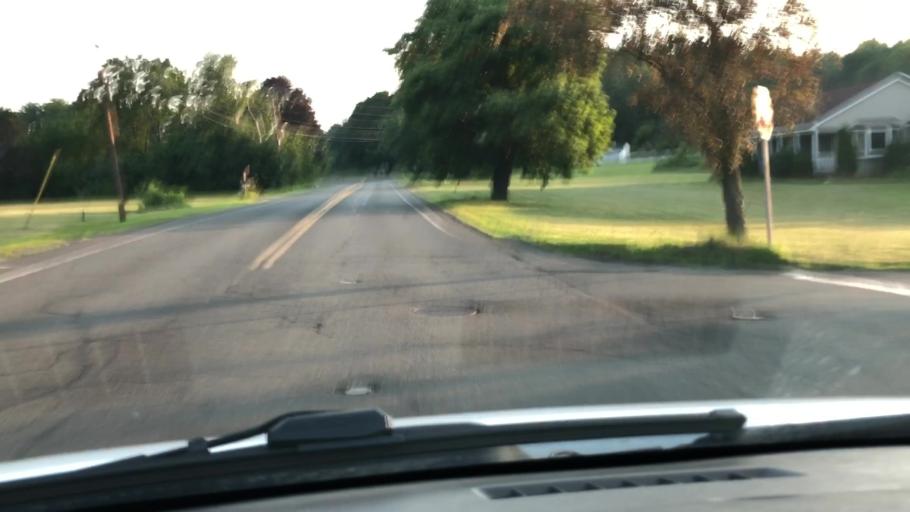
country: US
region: Massachusetts
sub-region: Hampshire County
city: Easthampton
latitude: 42.2883
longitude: -72.6723
